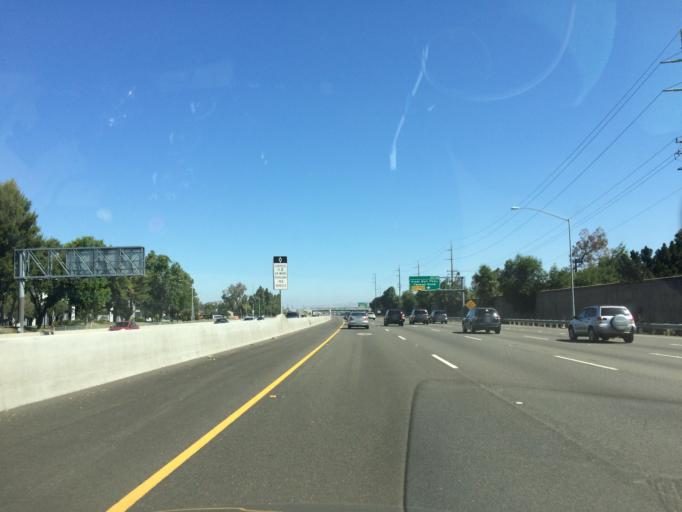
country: US
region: California
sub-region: Santa Clara County
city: Milpitas
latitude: 37.4077
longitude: -121.9104
